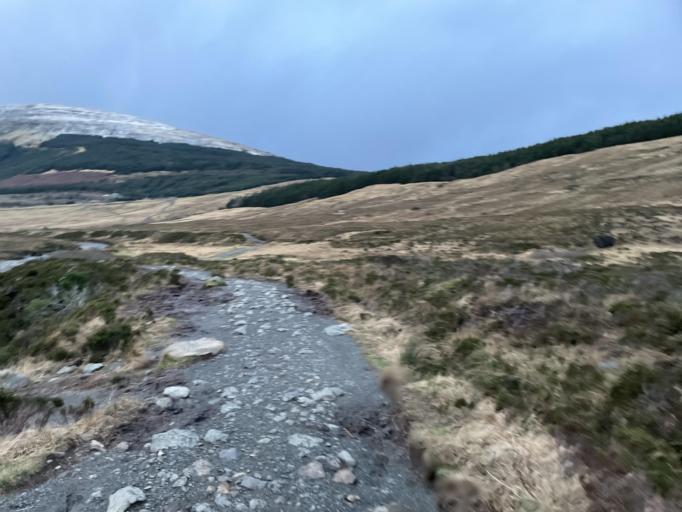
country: GB
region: Scotland
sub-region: Highland
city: Isle of Skye
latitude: 57.2505
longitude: -6.2569
